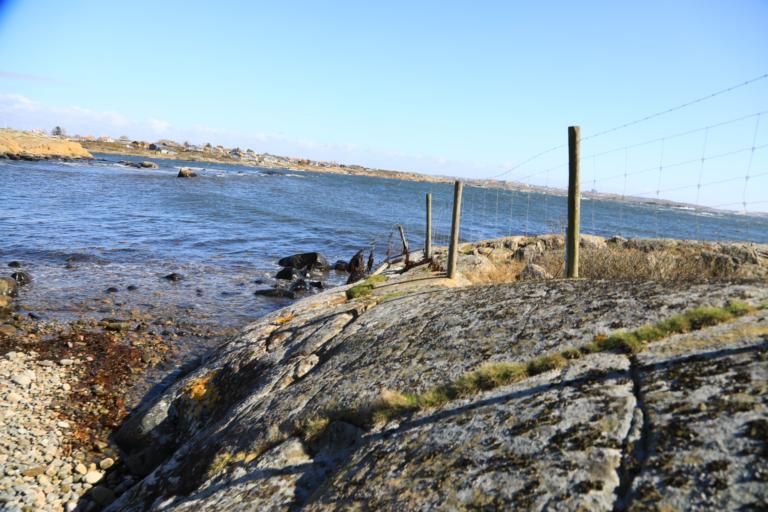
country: SE
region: Halland
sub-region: Varbergs Kommun
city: Varberg
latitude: 57.1169
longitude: 12.1995
